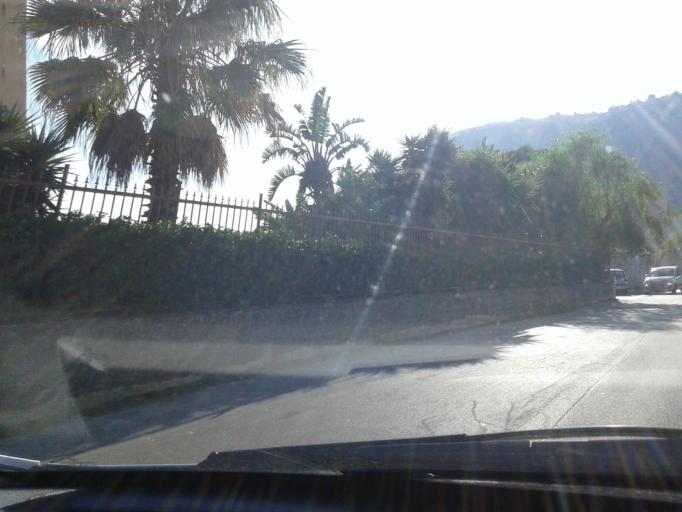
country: IT
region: Sicily
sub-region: Palermo
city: Palermo
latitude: 38.1033
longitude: 13.3169
